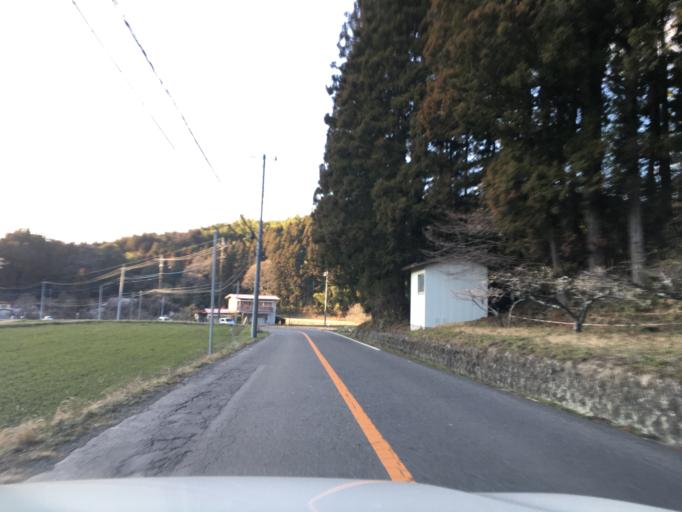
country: JP
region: Tochigi
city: Otawara
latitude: 36.8605
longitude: 140.1732
